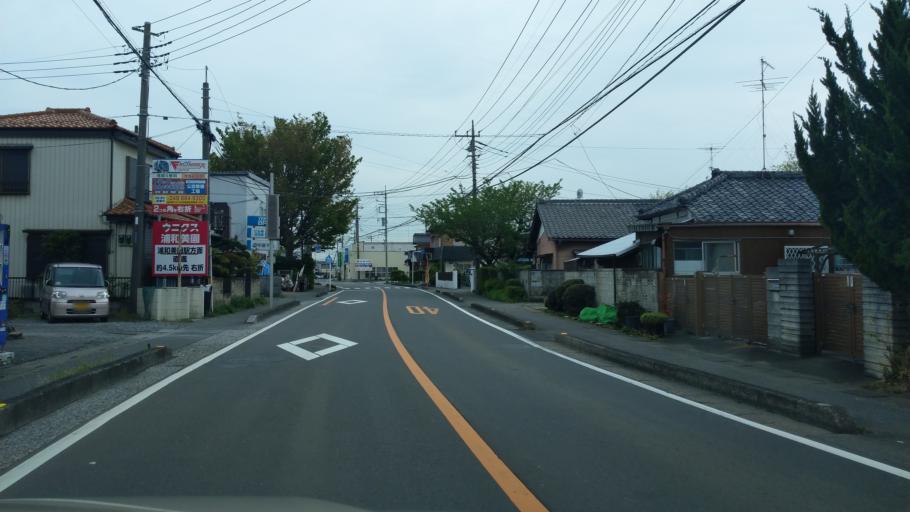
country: JP
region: Saitama
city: Iwatsuki
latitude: 35.9407
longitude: 139.7094
